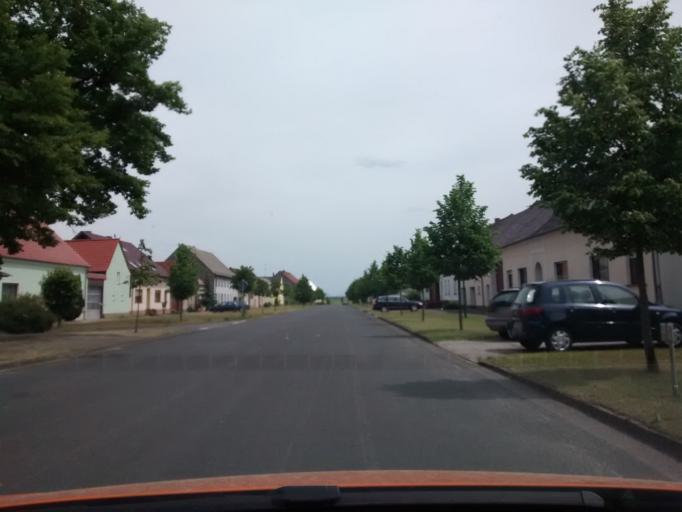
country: DE
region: Brandenburg
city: Ihlow
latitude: 51.8478
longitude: 13.2699
